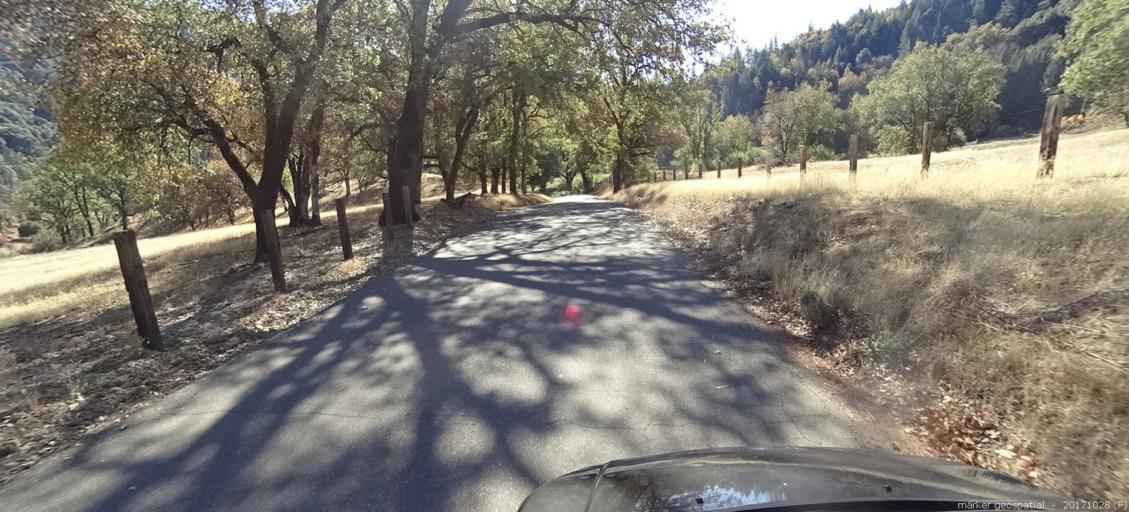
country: US
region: California
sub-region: Trinity County
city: Lewiston
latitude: 40.7911
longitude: -122.6131
